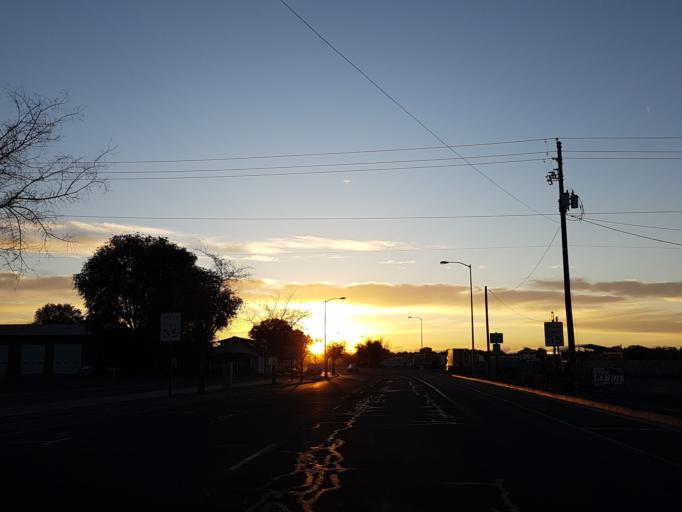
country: US
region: Oregon
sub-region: Malheur County
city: Vale
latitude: 43.9827
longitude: -117.2457
